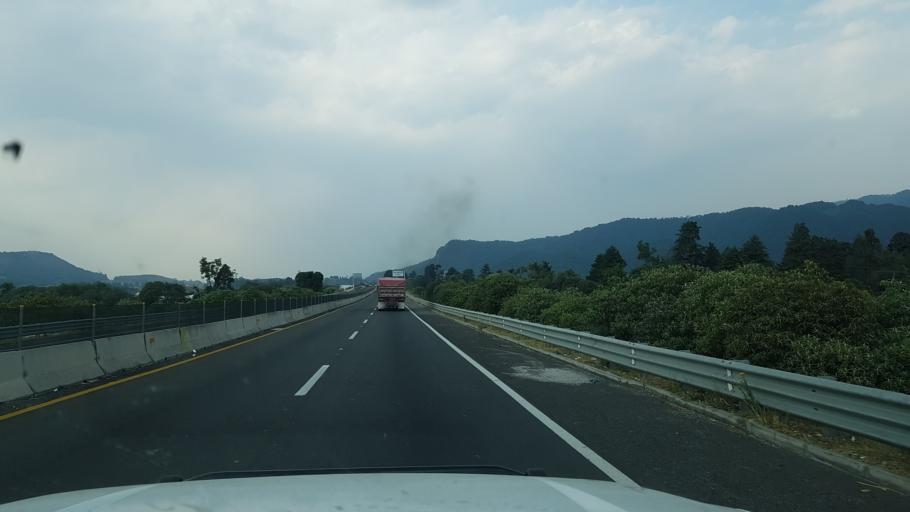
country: MX
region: Mexico
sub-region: Ayapango
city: La Colonia
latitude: 19.1411
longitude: -98.7760
